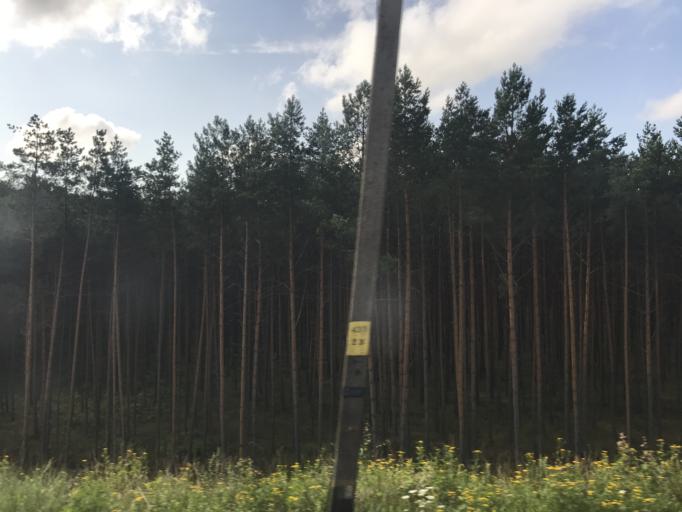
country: PL
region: Kujawsko-Pomorskie
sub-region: Powiat swiecki
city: Warlubie
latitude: 53.5602
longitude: 18.5729
